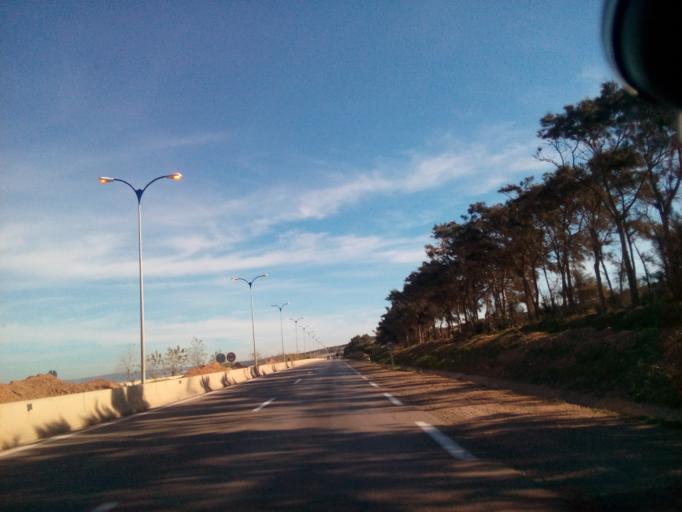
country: DZ
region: Mostaganem
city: Mostaganem
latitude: 35.8040
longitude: -0.0568
